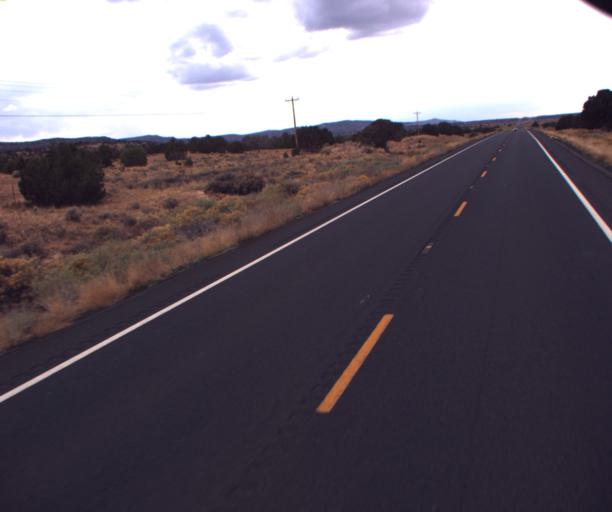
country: US
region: Arizona
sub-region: Coconino County
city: Kaibito
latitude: 36.4739
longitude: -110.6619
